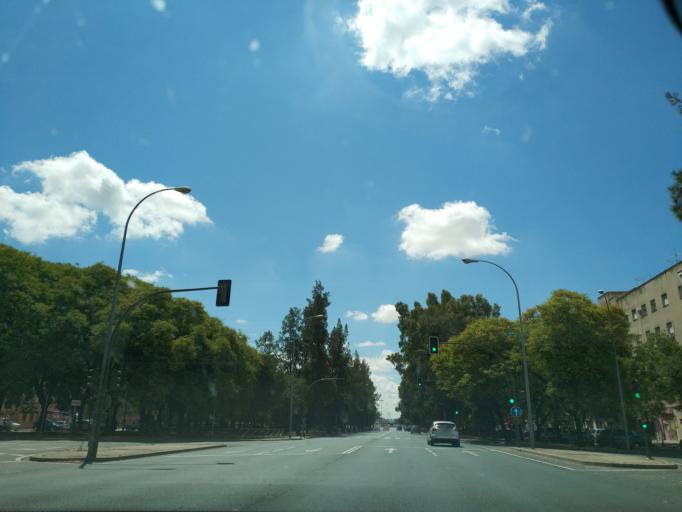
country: ES
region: Andalusia
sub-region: Provincia de Sevilla
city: Sevilla
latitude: 37.3634
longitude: -5.9619
